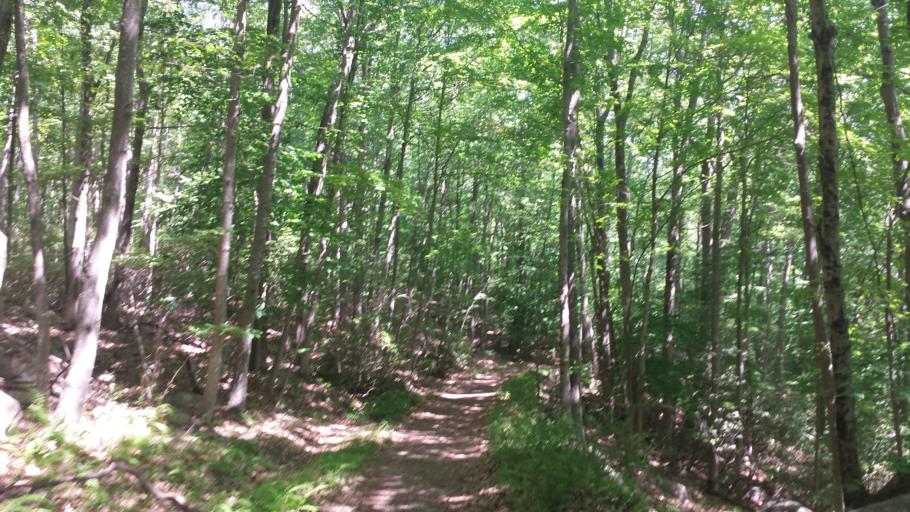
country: US
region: New York
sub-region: Westchester County
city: Pound Ridge
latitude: 41.2526
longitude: -73.5692
